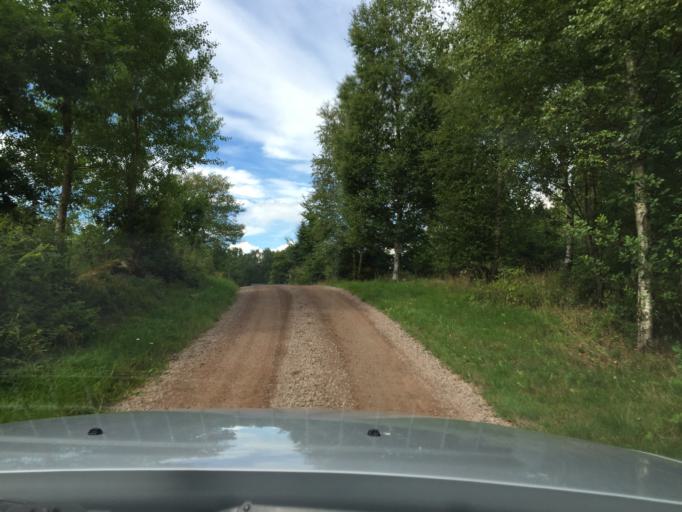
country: SE
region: Skane
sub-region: Hassleholms Kommun
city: Sosdala
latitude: 56.0296
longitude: 13.6390
